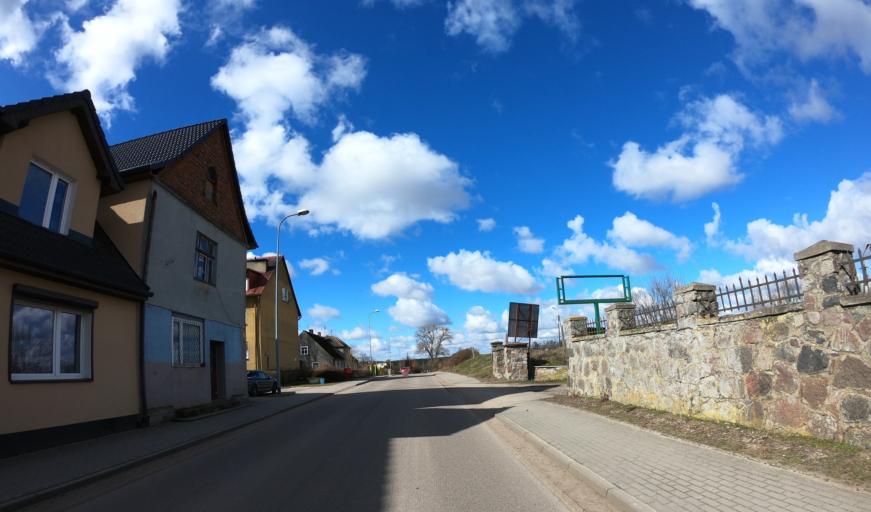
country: PL
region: West Pomeranian Voivodeship
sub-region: Powiat drawski
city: Drawsko Pomorskie
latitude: 53.4935
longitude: 15.8555
